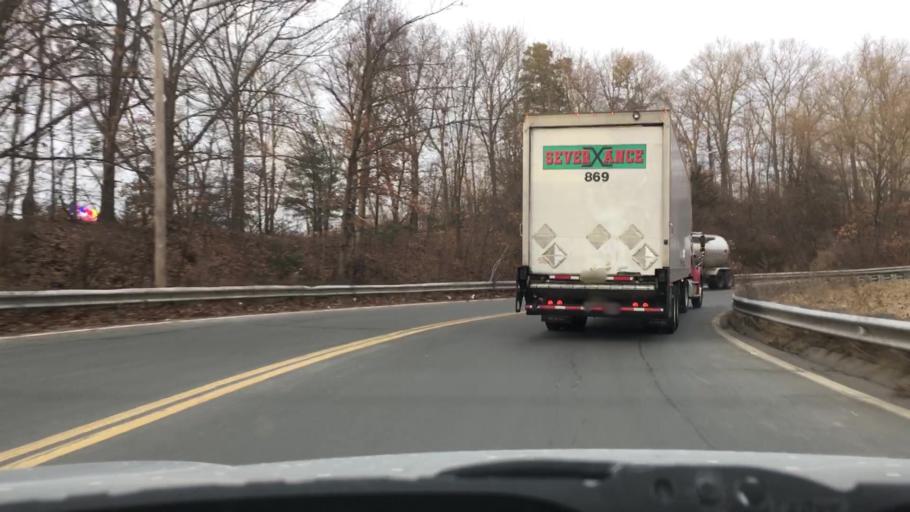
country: US
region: Massachusetts
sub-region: Hampden County
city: North Chicopee
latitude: 42.1601
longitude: -72.5496
